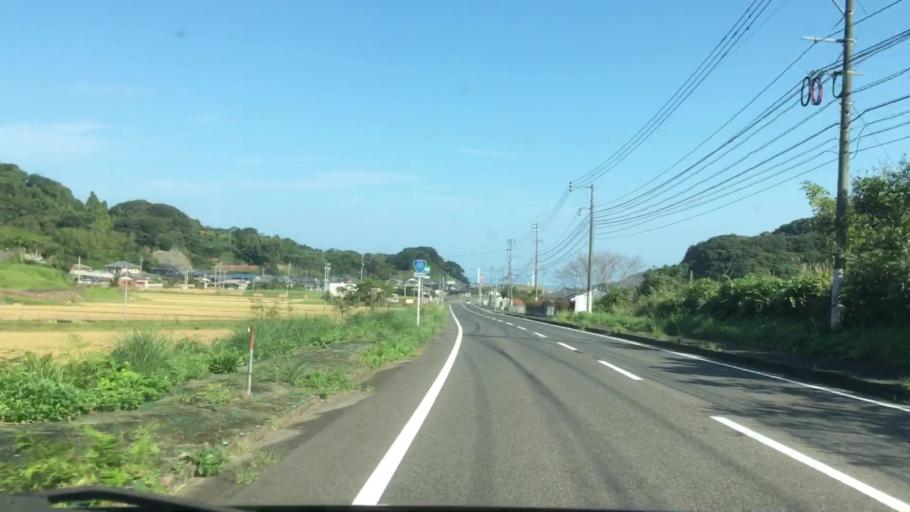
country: JP
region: Nagasaki
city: Sasebo
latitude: 32.9846
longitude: 129.6460
